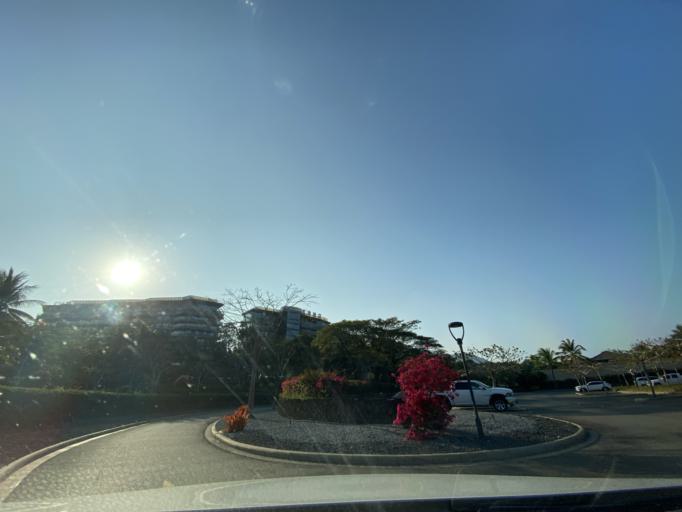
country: CN
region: Hainan
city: Xincun
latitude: 18.4185
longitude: 109.9510
